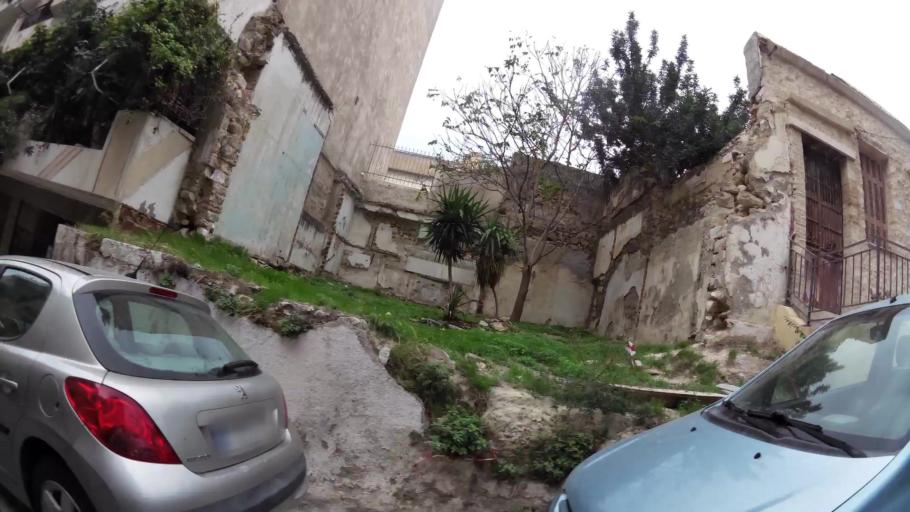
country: GR
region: Attica
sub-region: Nomos Attikis
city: Piraeus
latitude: 37.9474
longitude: 23.6521
